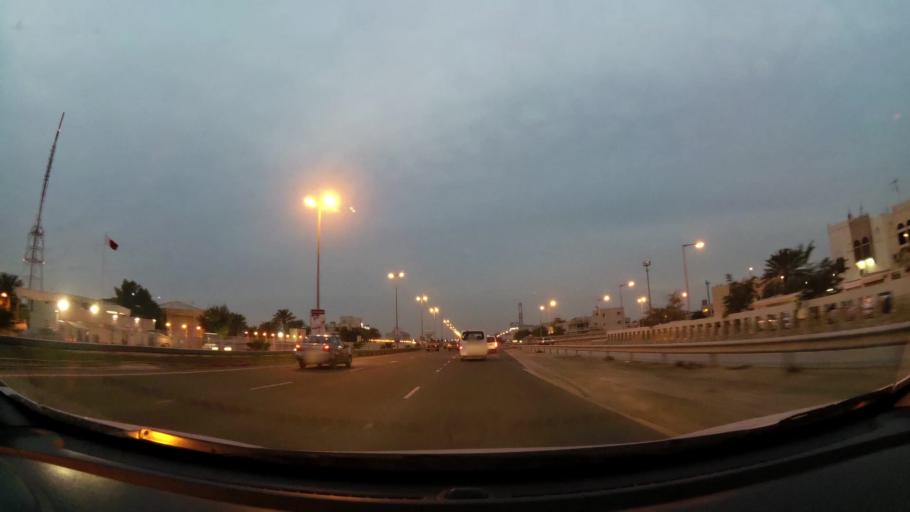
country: BH
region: Northern
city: Madinat `Isa
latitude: 26.1643
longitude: 50.5563
